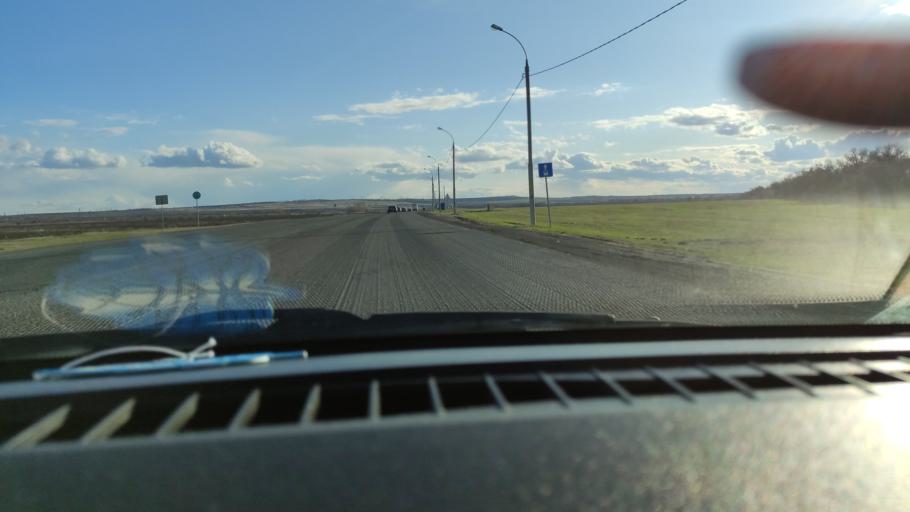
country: RU
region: Saratov
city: Yelshanka
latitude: 51.8128
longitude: 46.2046
